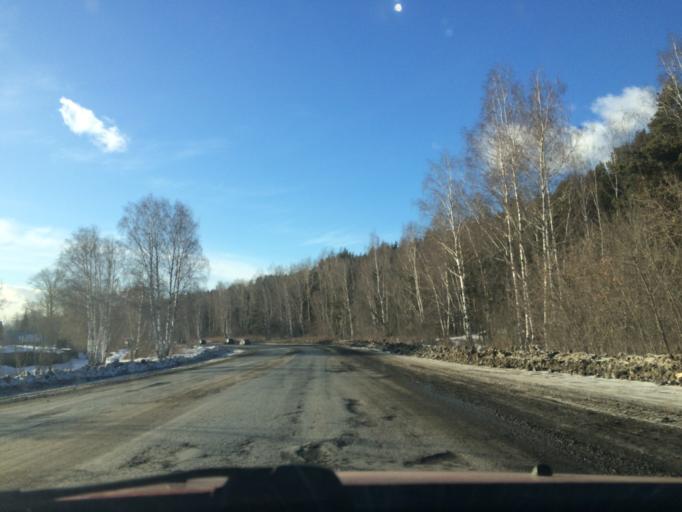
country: RU
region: Sverdlovsk
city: Istok
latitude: 56.7868
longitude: 60.7589
